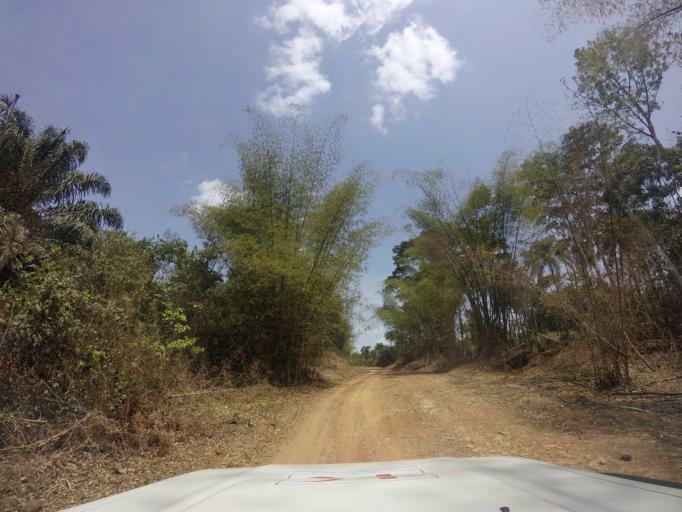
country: SL
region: Southern Province
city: Zimmi
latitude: 7.1225
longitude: -11.2818
